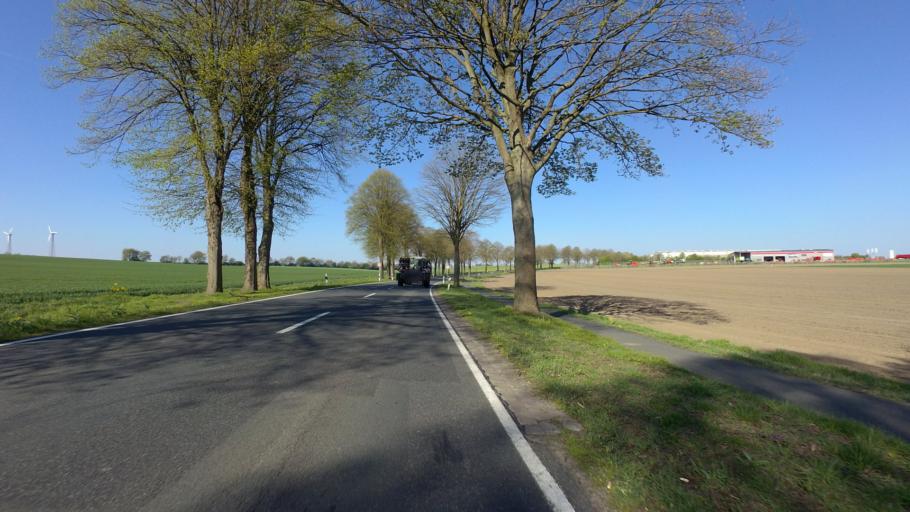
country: DE
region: Lower Saxony
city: Steimbke
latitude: 52.6517
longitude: 9.4126
